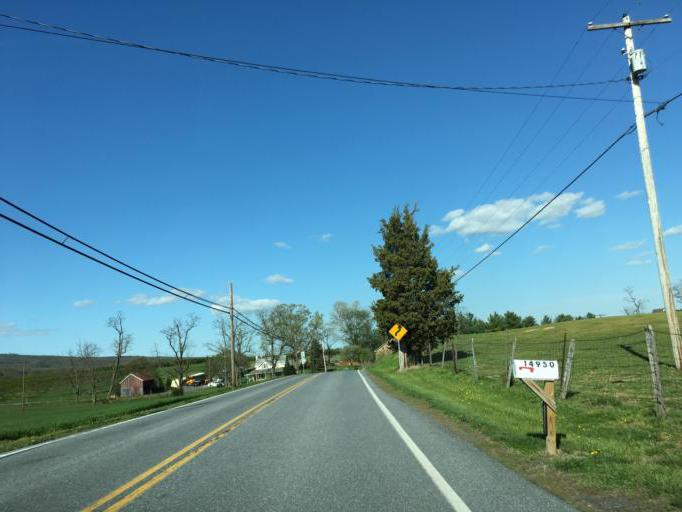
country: US
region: Maryland
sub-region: Frederick County
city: Thurmont
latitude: 39.6477
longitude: -77.3995
